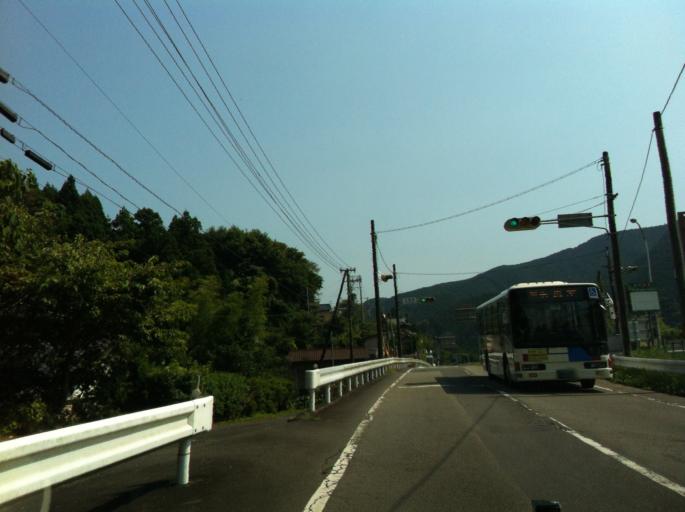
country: JP
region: Shizuoka
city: Shizuoka-shi
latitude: 35.1137
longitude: 138.3610
